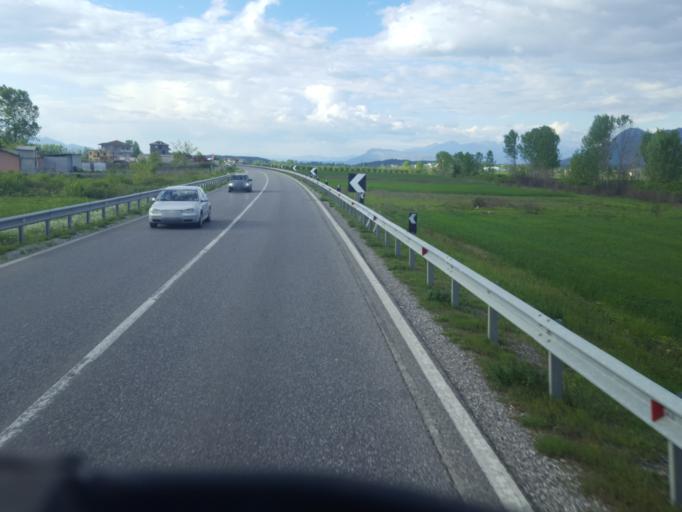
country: AL
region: Lezhe
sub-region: Rrethi i Lezhes
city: Balldreni i Ri
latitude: 41.8635
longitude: 19.6375
